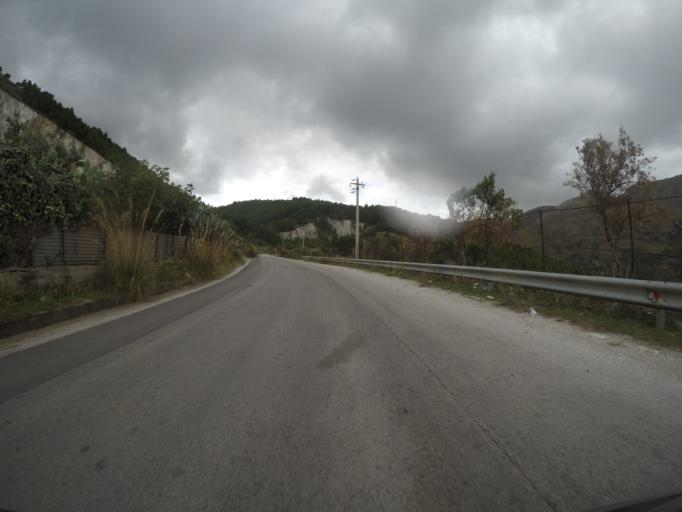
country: IT
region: Sicily
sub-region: Palermo
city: Montelepre
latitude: 38.1172
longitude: 13.1721
